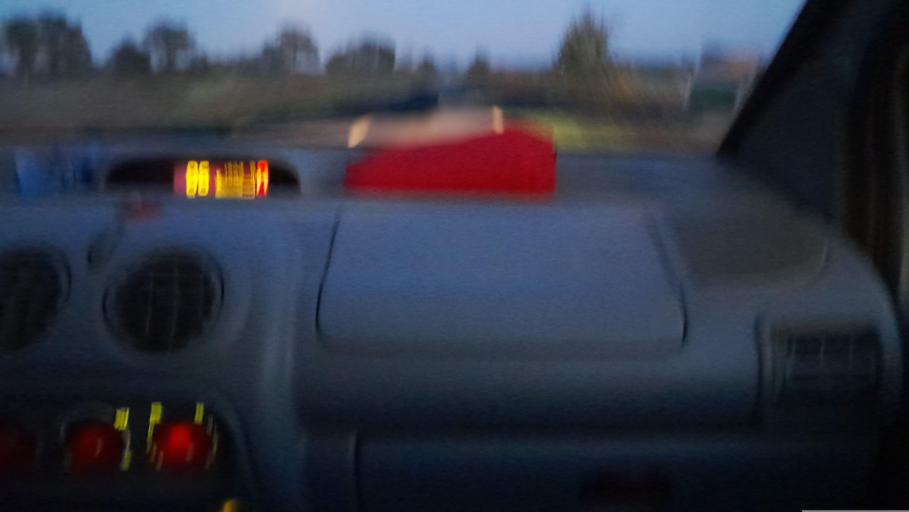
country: FR
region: Pays de la Loire
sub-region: Departement de la Mayenne
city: Ballots
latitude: 47.9017
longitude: -1.1315
